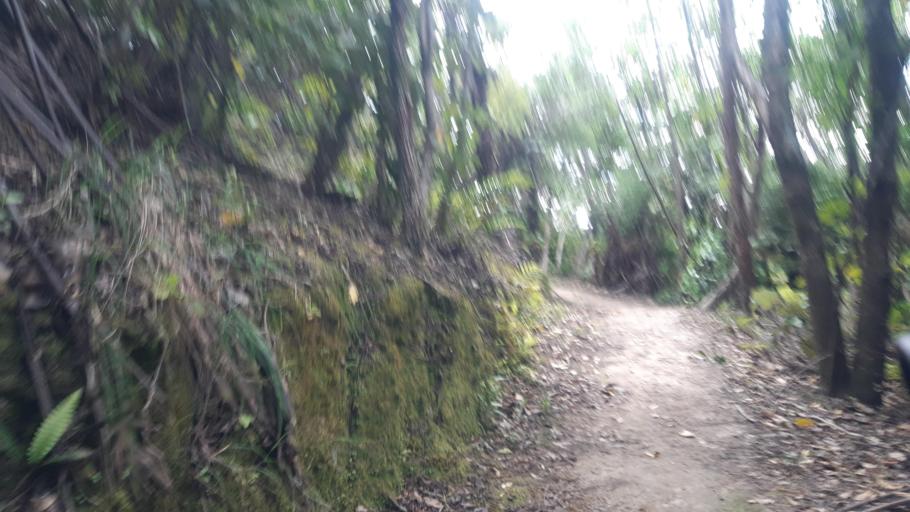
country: NZ
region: Marlborough
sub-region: Marlborough District
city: Picton
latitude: -41.2841
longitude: 174.0138
